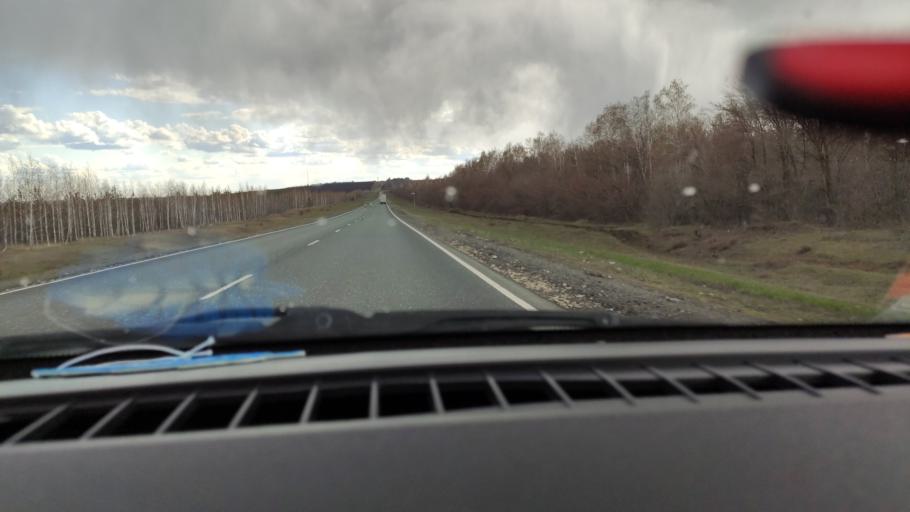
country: RU
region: Saratov
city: Balakovo
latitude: 52.1473
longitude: 47.8077
